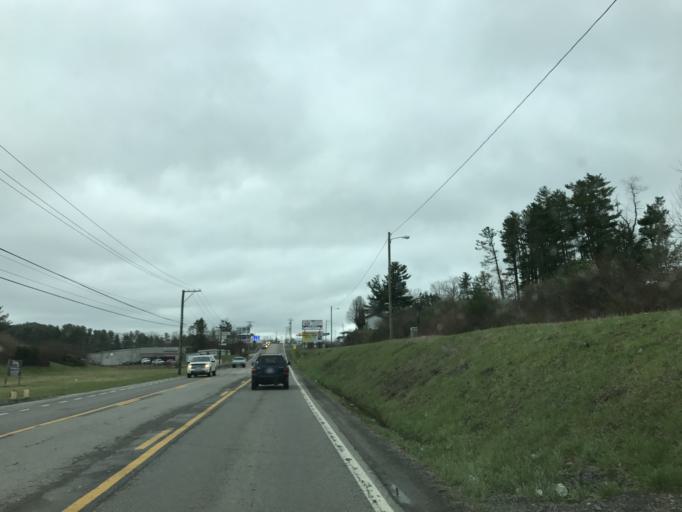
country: US
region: West Virginia
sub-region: Raleigh County
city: Beckley
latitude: 37.7973
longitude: -81.1762
